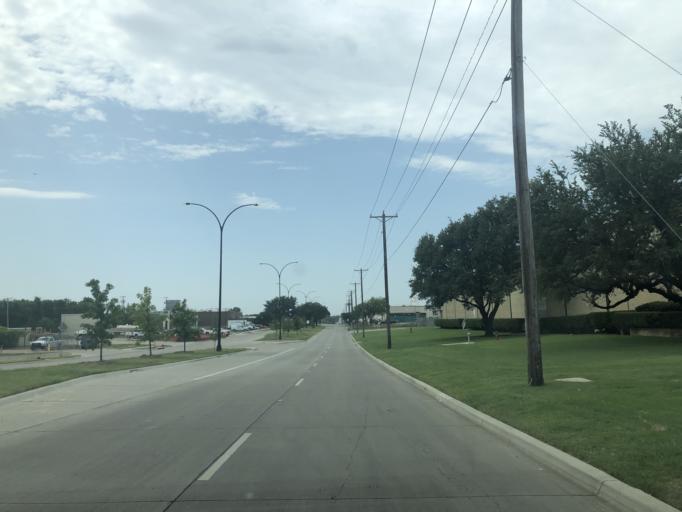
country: US
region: Texas
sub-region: Dallas County
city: Grand Prairie
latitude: 32.7563
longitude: -97.0459
